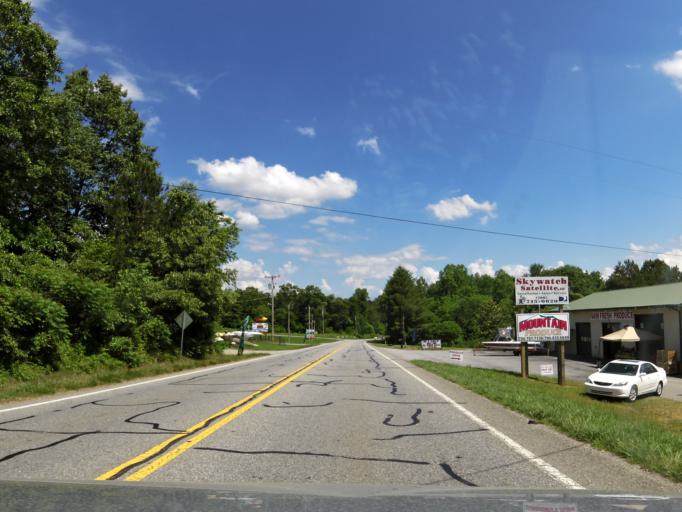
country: US
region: Georgia
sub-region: Union County
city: Blairsville
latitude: 34.8910
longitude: -83.9917
